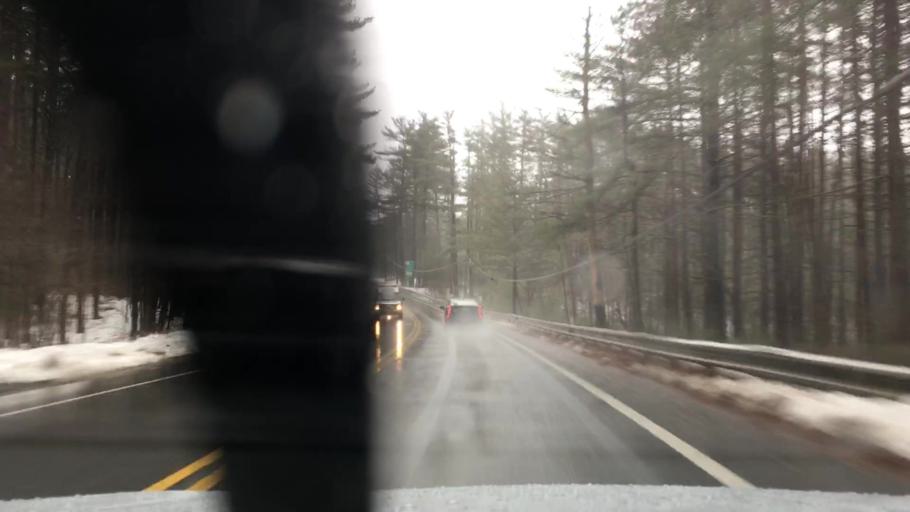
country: US
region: Massachusetts
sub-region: Franklin County
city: Orange
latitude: 42.5362
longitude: -72.3070
